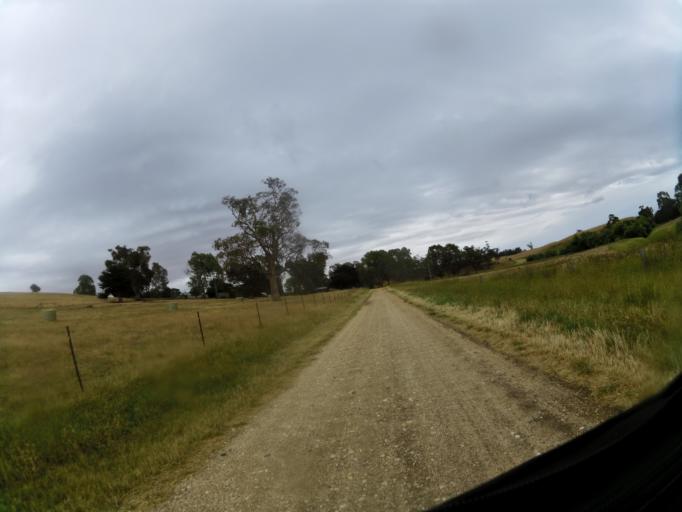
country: AU
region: Victoria
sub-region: Mount Alexander
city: Castlemaine
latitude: -37.2011
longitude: 144.0159
